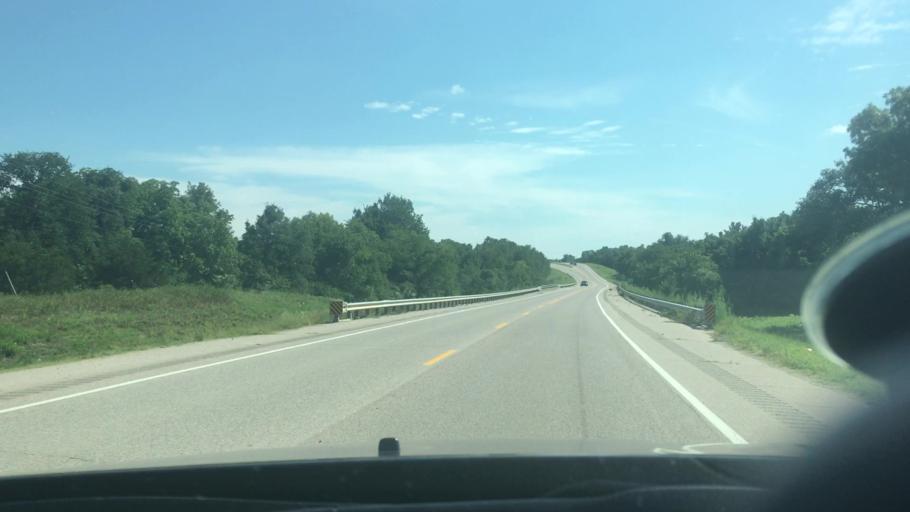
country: US
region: Oklahoma
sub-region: Seminole County
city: Konawa
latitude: 34.9496
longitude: -96.6800
